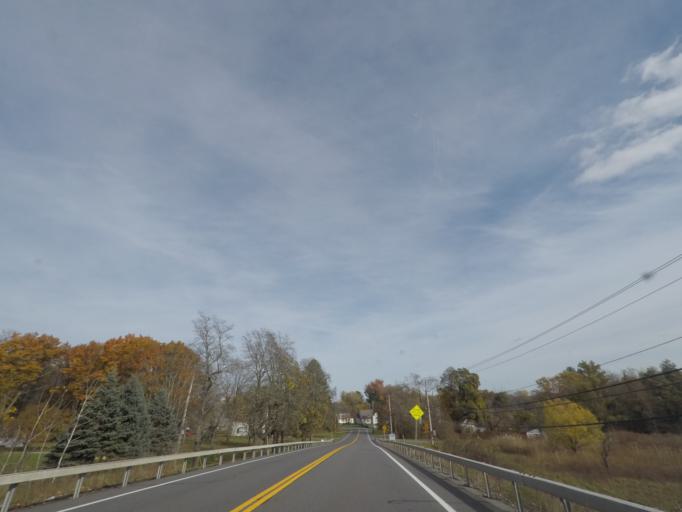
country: US
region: New York
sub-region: Schenectady County
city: Rotterdam
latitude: 42.7667
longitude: -73.9817
